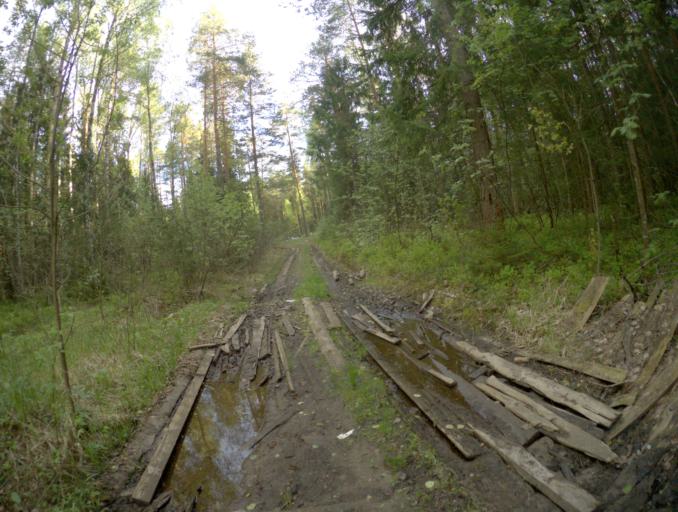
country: RU
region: Vladimir
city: Anopino
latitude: 55.7206
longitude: 40.6130
